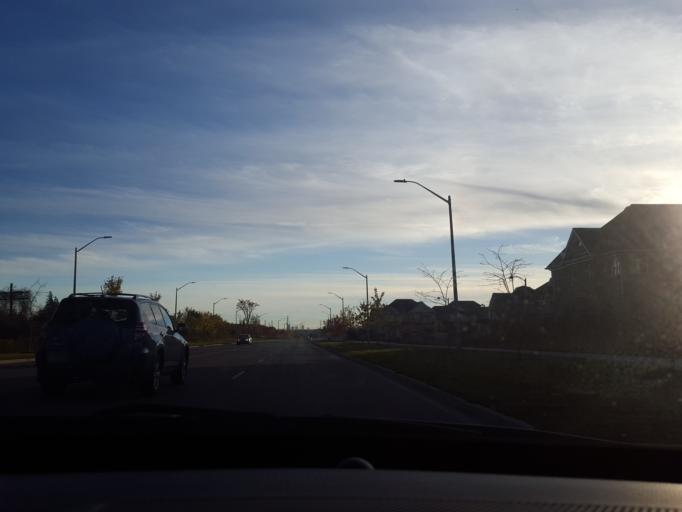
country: CA
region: Ontario
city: Markham
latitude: 43.8664
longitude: -79.2126
